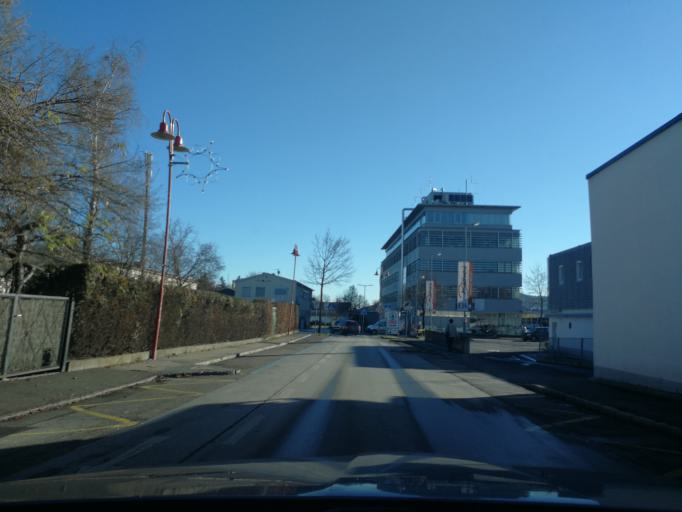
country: AT
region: Styria
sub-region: Politischer Bezirk Weiz
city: Gleisdorf
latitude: 47.1039
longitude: 15.7088
